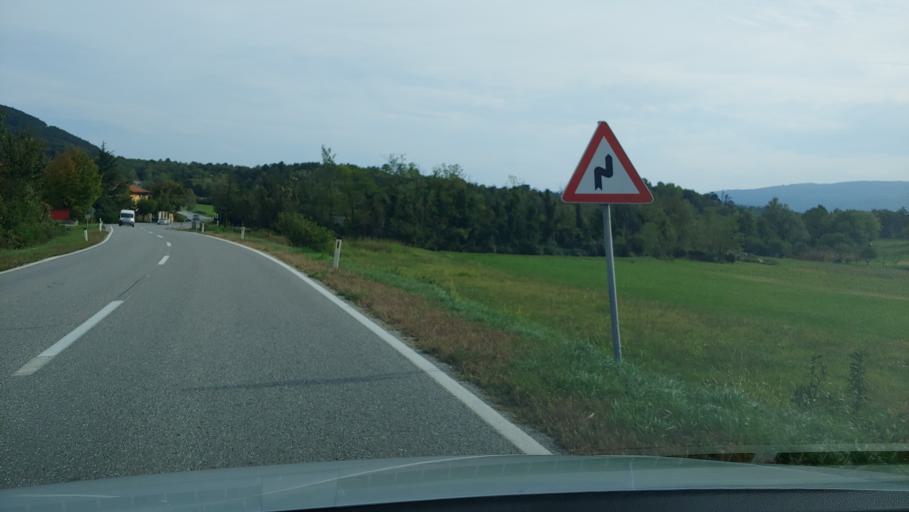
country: SI
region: Nova Gorica
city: Sempas
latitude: 45.9206
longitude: 13.7566
